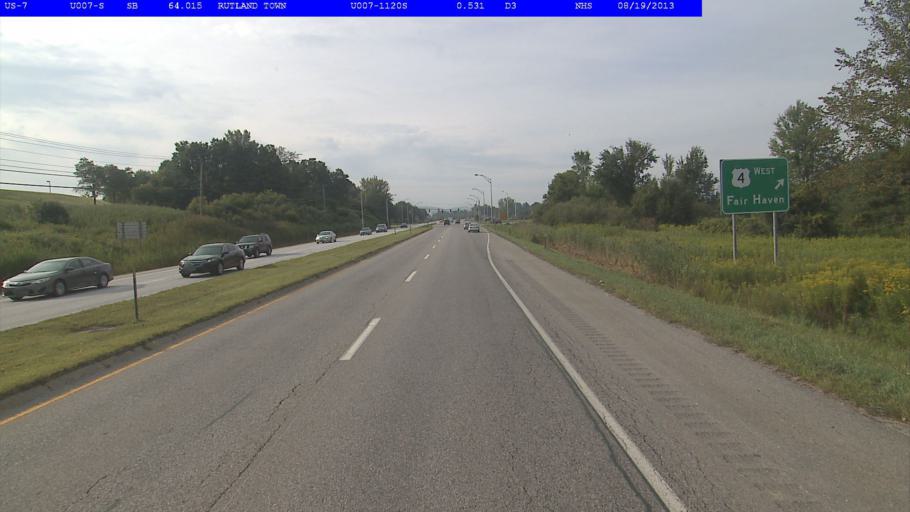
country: US
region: Vermont
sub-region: Rutland County
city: Rutland
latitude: 43.5811
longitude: -72.9673
